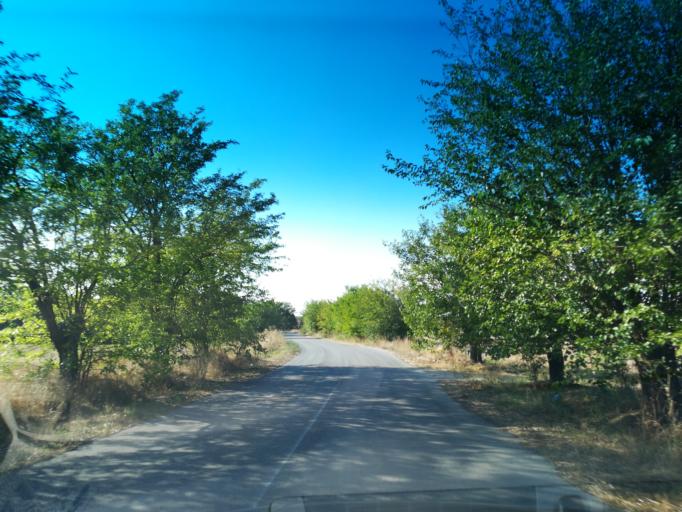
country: BG
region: Stara Zagora
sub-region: Obshtina Chirpan
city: Chirpan
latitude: 42.0555
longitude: 25.2700
